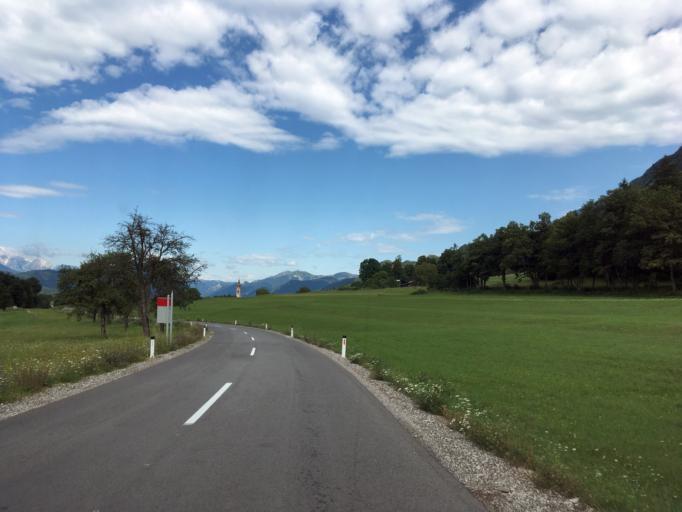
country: SI
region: Radovljica
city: Lesce
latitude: 46.3793
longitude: 14.1829
